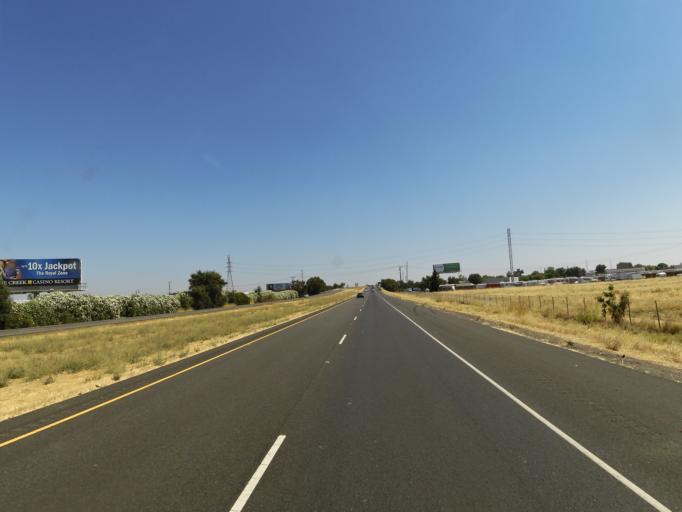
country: US
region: California
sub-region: Yolo County
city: Woodland
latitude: 38.6830
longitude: -121.7501
